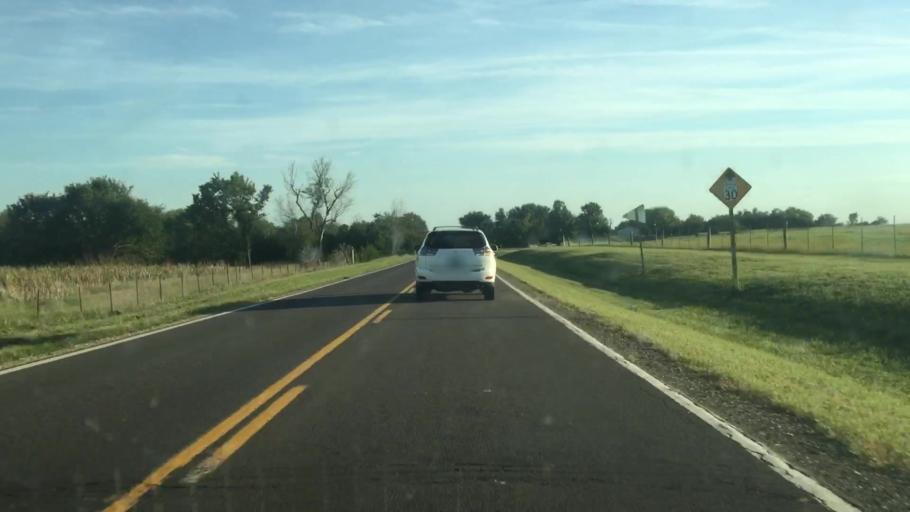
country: US
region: Kansas
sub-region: Brown County
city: Horton
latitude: 39.5600
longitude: -95.5247
